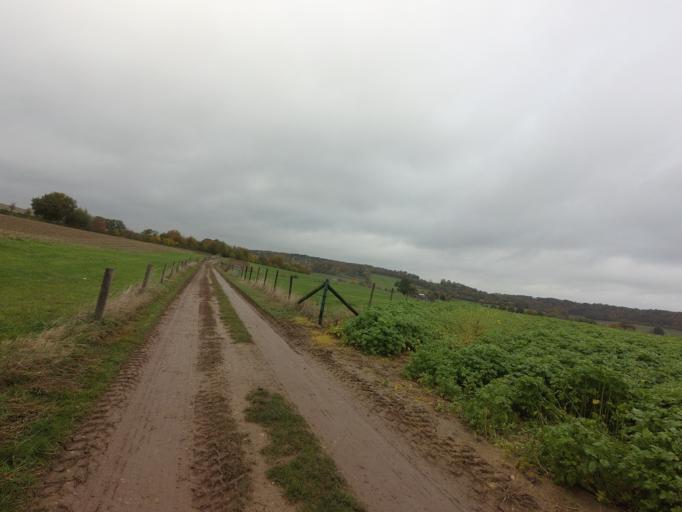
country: NL
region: Limburg
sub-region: Gemeente Simpelveld
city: Simpelveld
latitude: 50.7924
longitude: 5.9732
